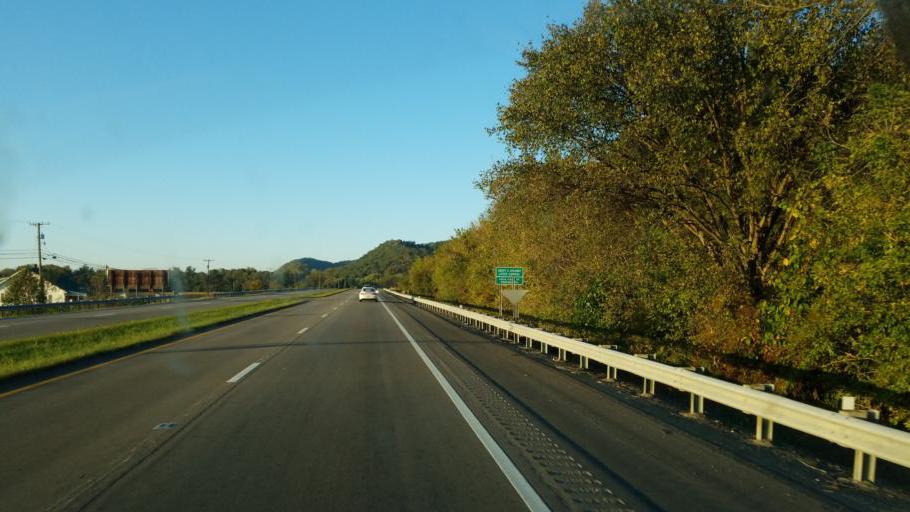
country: US
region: Ohio
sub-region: Scioto County
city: Rosemount
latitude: 38.8166
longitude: -82.9843
